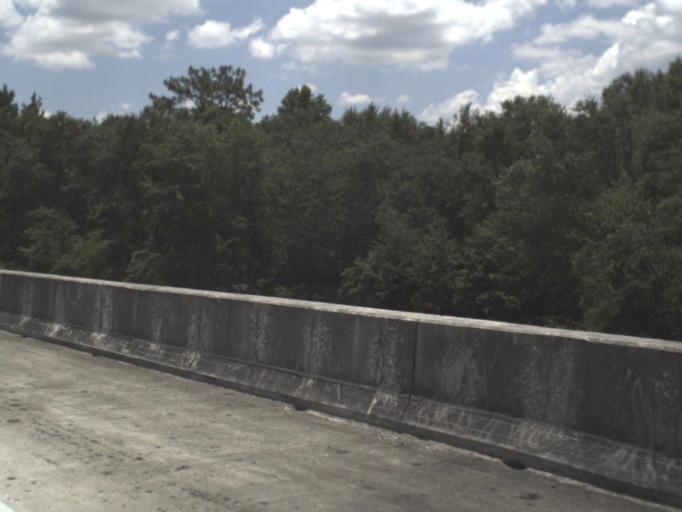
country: US
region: Florida
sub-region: Madison County
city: Madison
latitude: 30.3613
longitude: -83.2141
